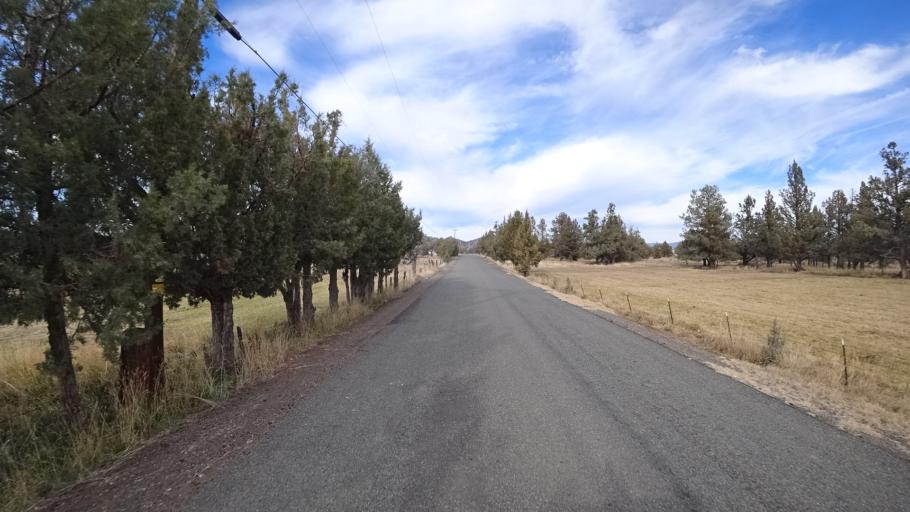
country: US
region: California
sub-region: Siskiyou County
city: Montague
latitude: 41.6409
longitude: -122.4190
